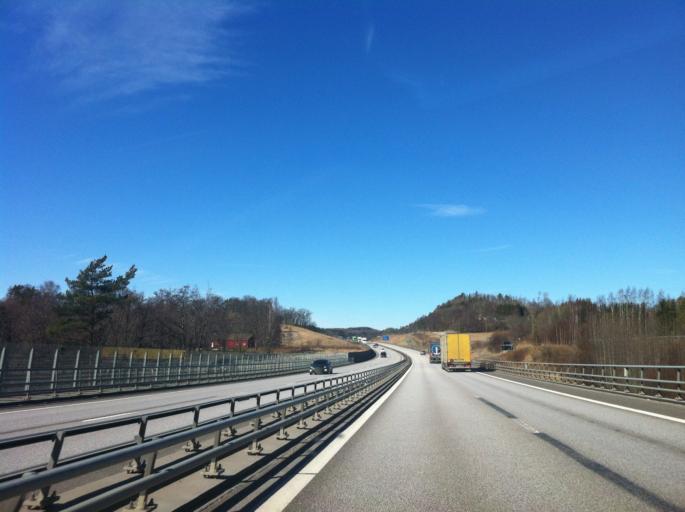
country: SE
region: Vaestra Goetaland
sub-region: Munkedals Kommun
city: Munkedal
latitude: 58.3799
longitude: 11.7751
